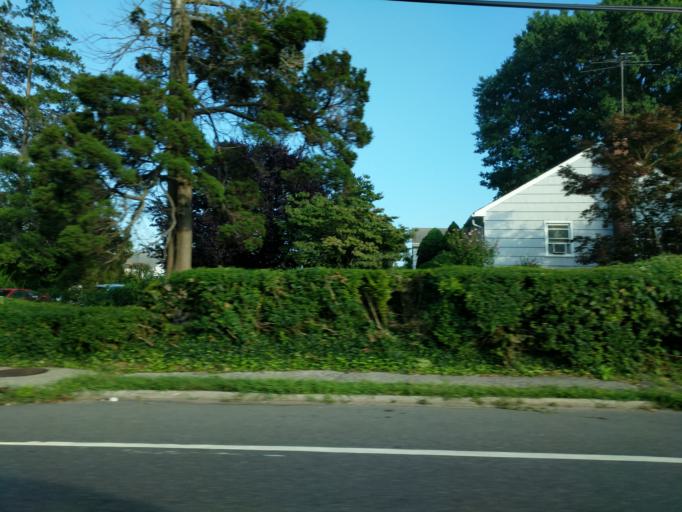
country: US
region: New York
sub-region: Nassau County
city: Hewlett
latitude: 40.6490
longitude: -73.6916
